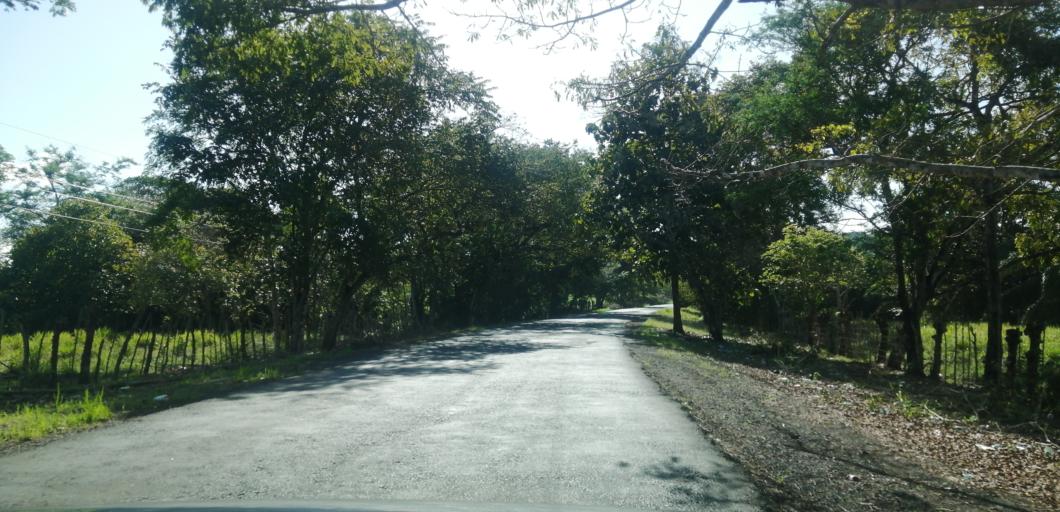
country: PA
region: Panama
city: Canita
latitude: 9.2174
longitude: -78.8370
